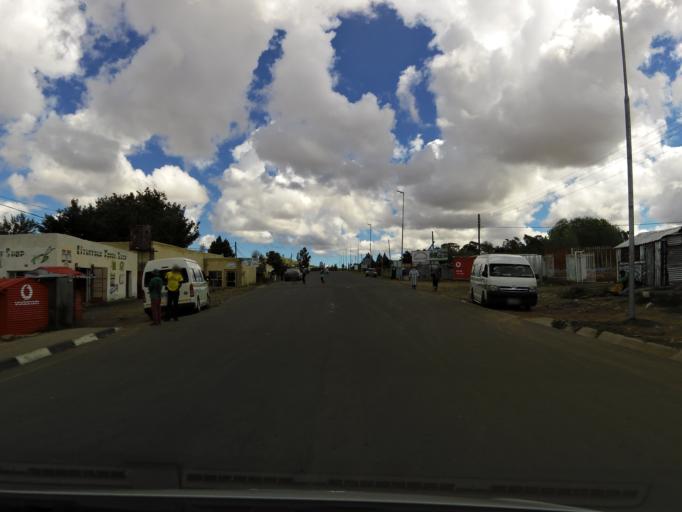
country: LS
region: Mafeteng
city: Mafeteng
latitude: -29.6910
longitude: 27.4360
